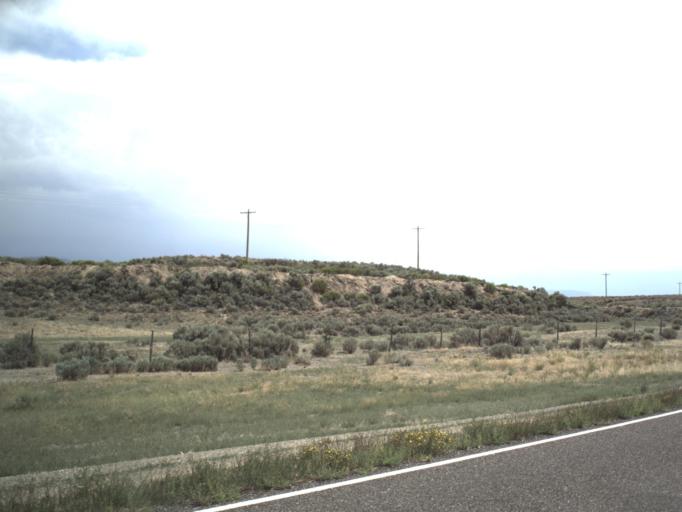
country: US
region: Utah
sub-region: Piute County
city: Junction
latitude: 38.1396
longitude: -111.9977
